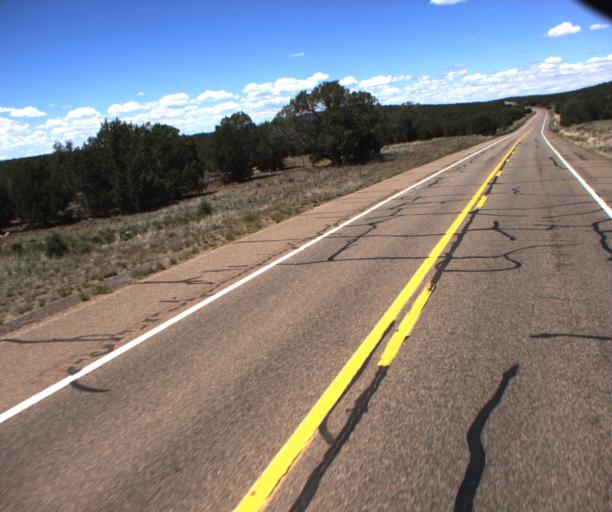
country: US
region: Arizona
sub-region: Yavapai County
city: Paulden
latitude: 35.1192
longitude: -112.4339
